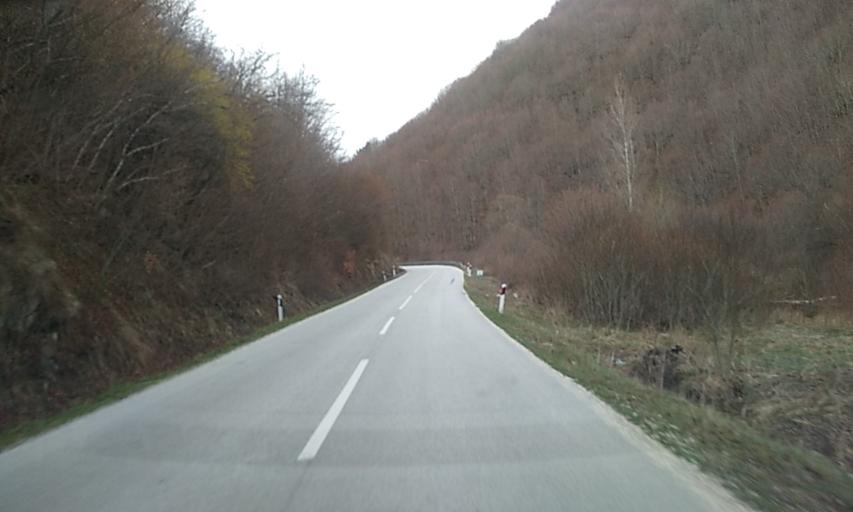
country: RS
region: Central Serbia
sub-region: Pcinjski Okrug
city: Bosilegrad
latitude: 42.5898
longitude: 22.4122
